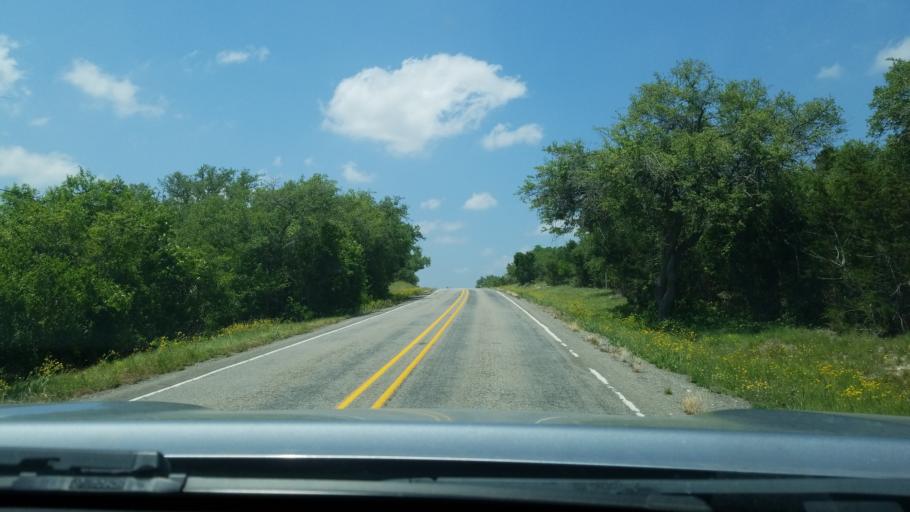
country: US
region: Texas
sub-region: Hays County
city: Woodcreek
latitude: 30.0572
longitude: -98.2067
